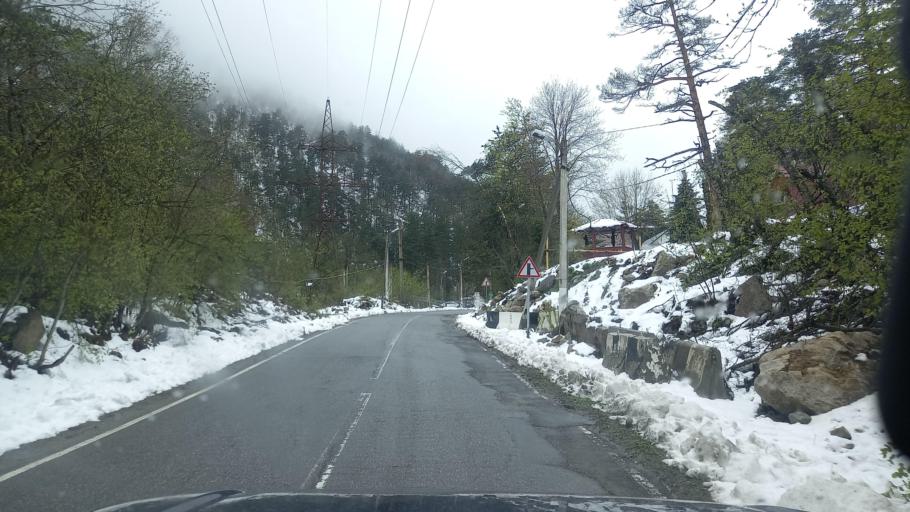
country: RU
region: North Ossetia
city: Mizur
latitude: 42.7939
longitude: 43.9238
